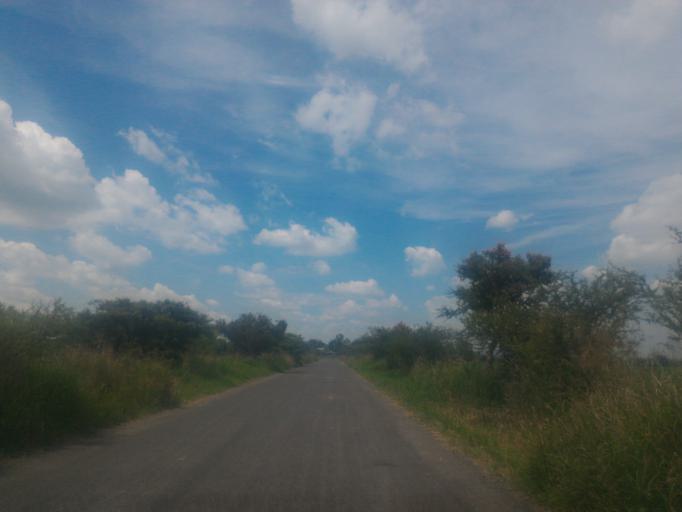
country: MX
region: Guanajuato
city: Ciudad Manuel Doblado
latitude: 20.8165
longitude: -102.0635
